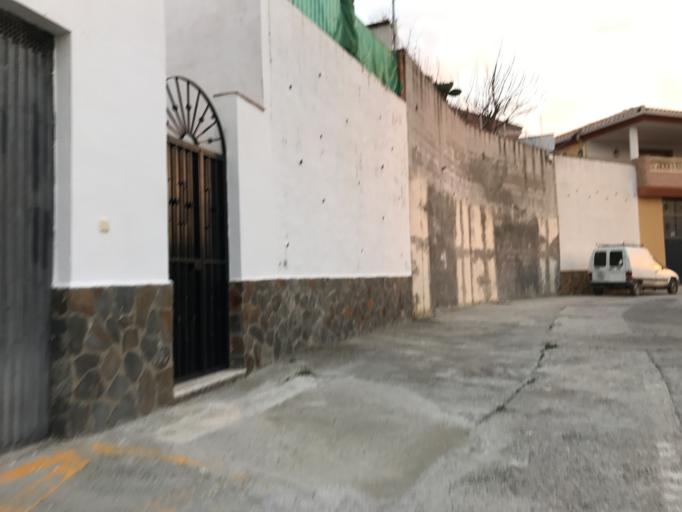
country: ES
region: Andalusia
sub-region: Provincia de Granada
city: Beas de Granada
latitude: 37.2188
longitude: -3.4790
